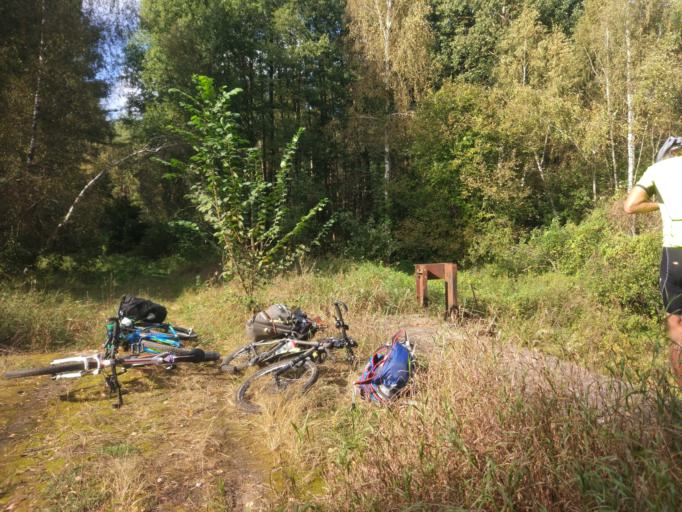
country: RU
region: Brjansk
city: Vyshkov
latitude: 52.5579
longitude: 31.6225
